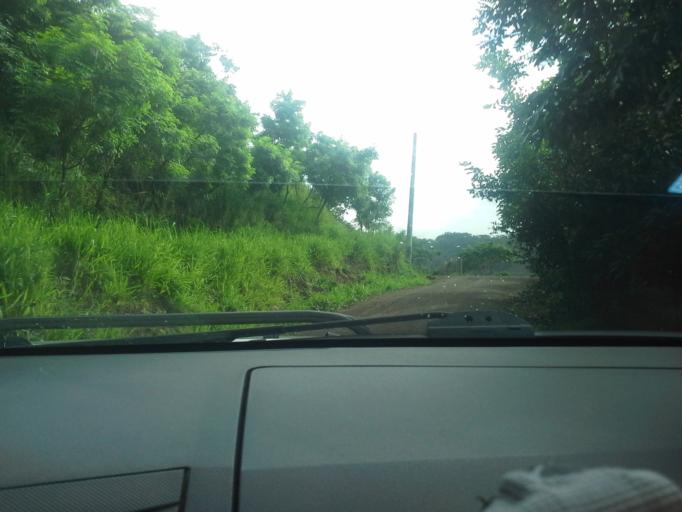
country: NI
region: Matagalpa
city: Matagalpa
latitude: 12.9212
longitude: -85.9320
